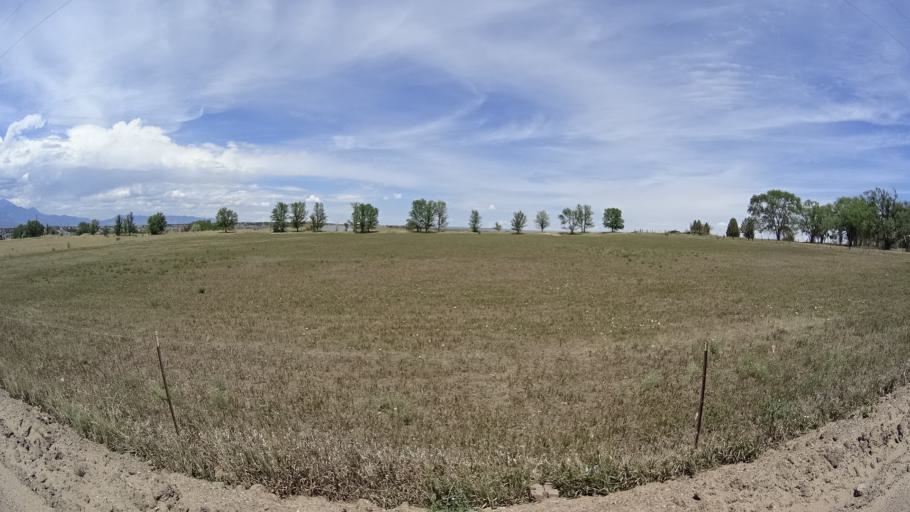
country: US
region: Colorado
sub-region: El Paso County
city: Fountain
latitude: 38.6940
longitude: -104.6696
